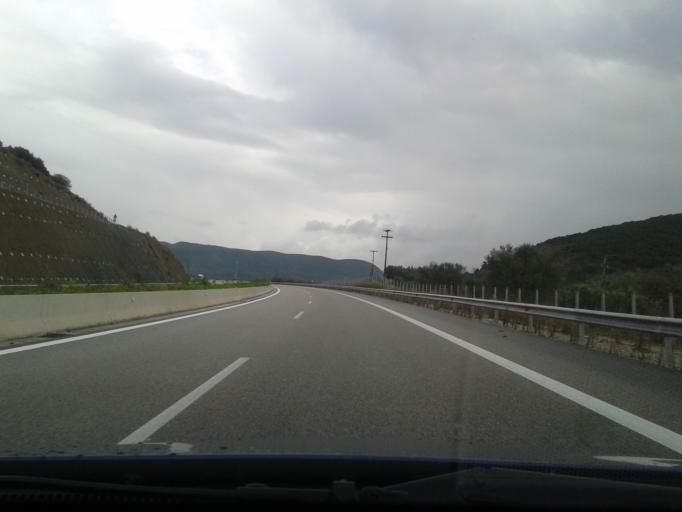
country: GR
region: West Greece
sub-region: Nomos Aitolias kai Akarnanias
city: Galatas
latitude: 38.3992
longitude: 21.5727
